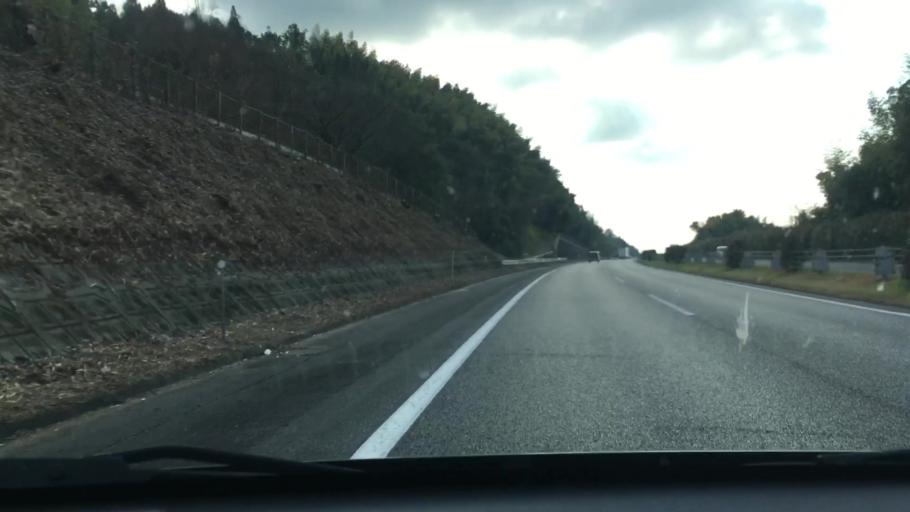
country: JP
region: Kumamoto
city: Yatsushiro
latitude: 32.5321
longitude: 130.6700
